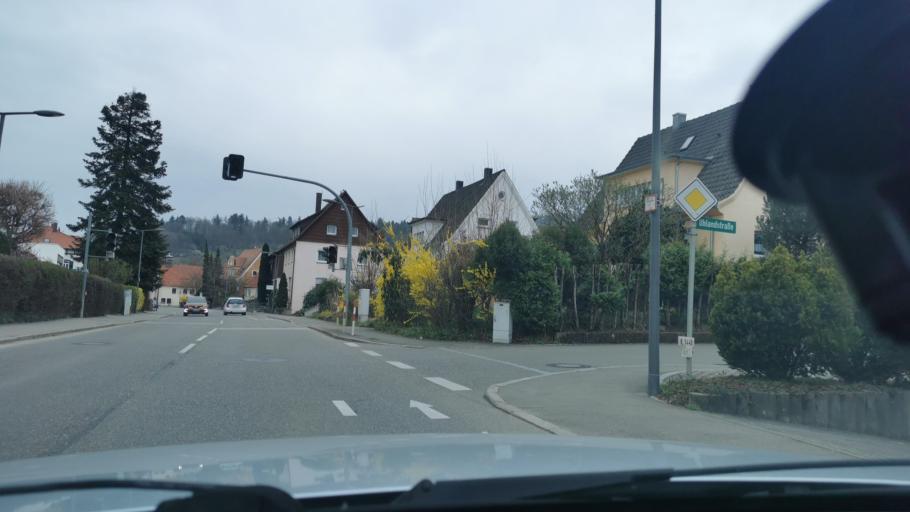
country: DE
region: Baden-Wuerttemberg
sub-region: Regierungsbezirk Stuttgart
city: Boll
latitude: 48.6380
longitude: 9.6080
